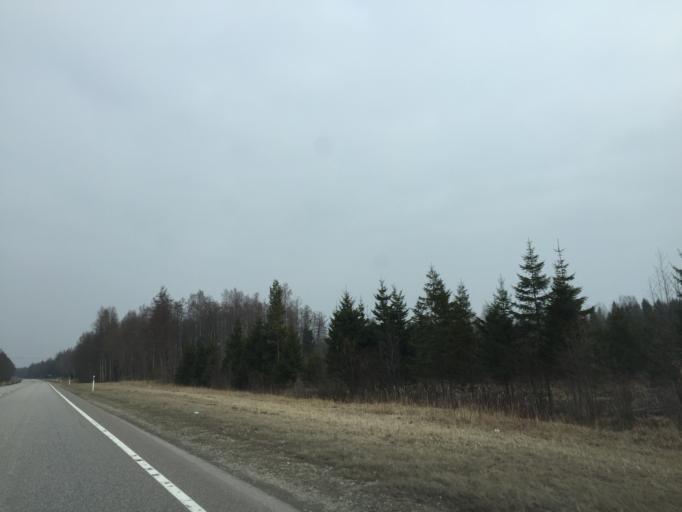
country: LV
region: Salacgrivas
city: Ainazi
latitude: 58.0477
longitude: 24.5100
